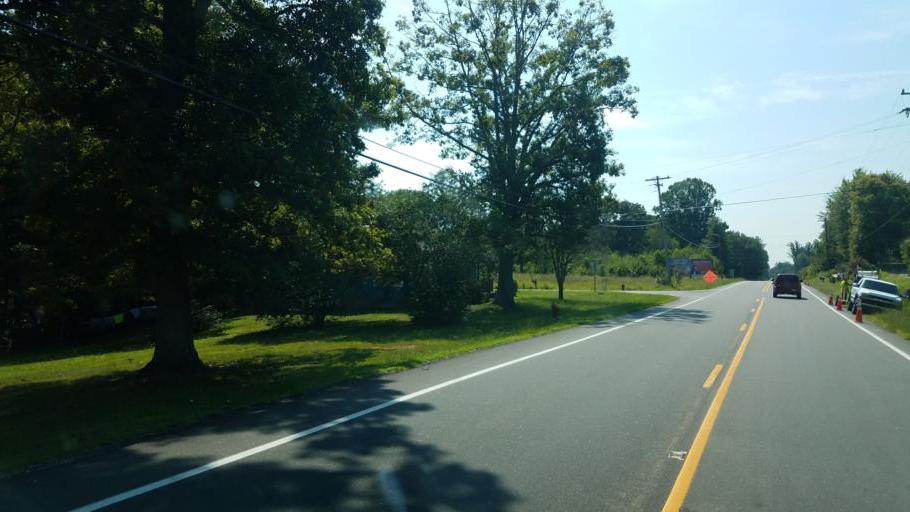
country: US
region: North Carolina
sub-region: Burke County
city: Glen Alpine
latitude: 35.7688
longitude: -81.7454
